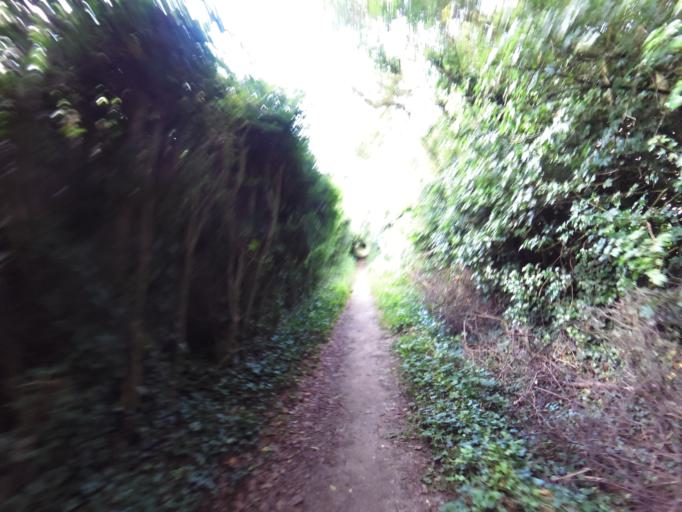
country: GB
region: England
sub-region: Suffolk
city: Ipswich
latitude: 52.0737
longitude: 1.1546
